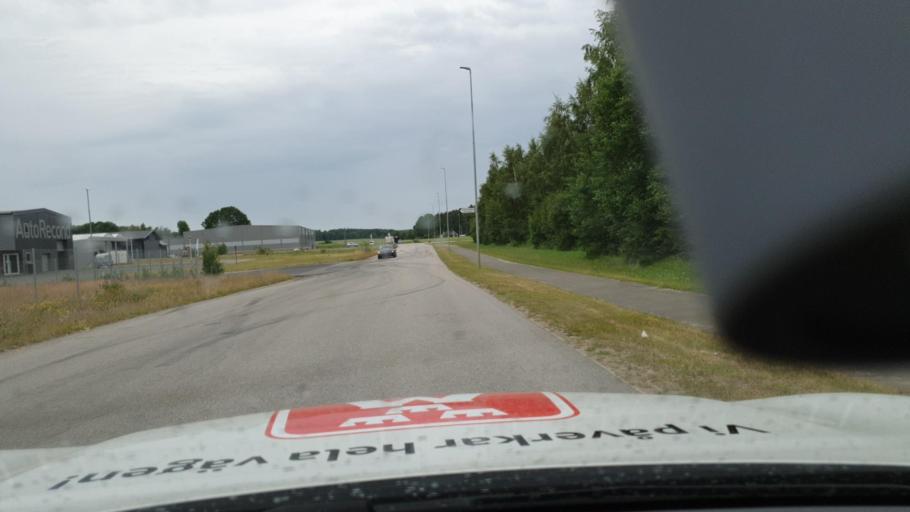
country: SE
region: Vaestra Goetaland
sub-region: Hjo Kommun
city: Hjo
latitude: 58.3154
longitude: 14.2984
